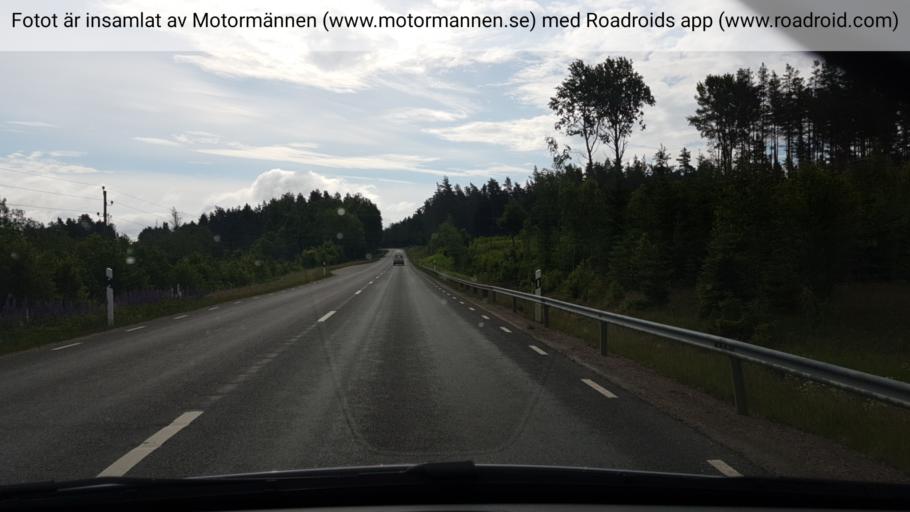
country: SE
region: Vaestra Goetaland
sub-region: Karlsborgs Kommun
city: Molltorp
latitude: 58.4893
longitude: 14.3871
